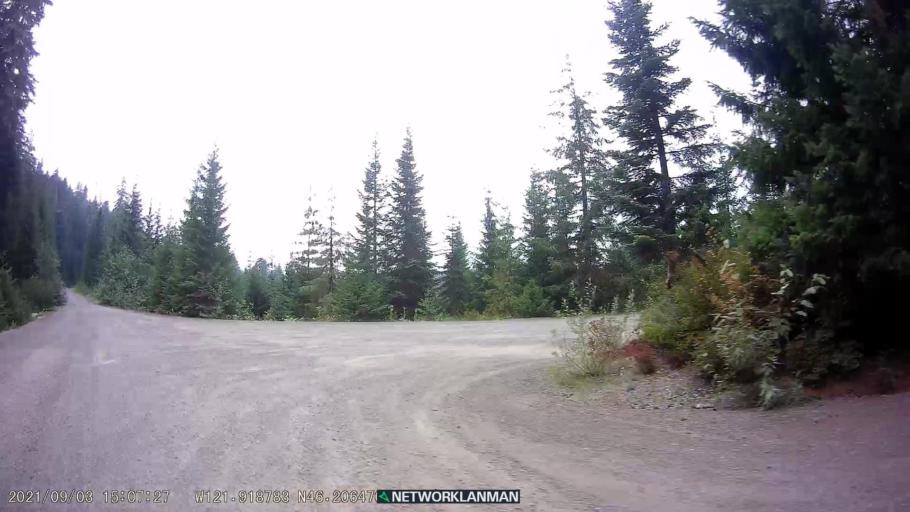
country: US
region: Washington
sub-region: Skamania County
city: Carson
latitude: 46.2063
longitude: -121.9189
